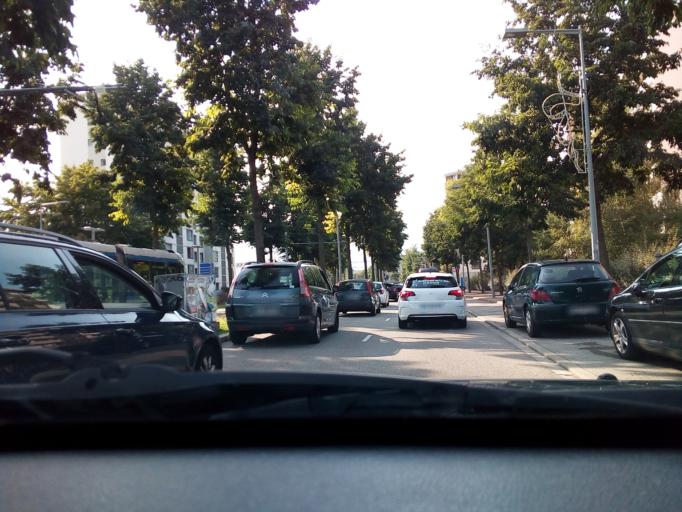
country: FR
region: Rhone-Alpes
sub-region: Departement de l'Isere
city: Saint-Martin-d'Heres
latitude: 45.1872
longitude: 5.7553
